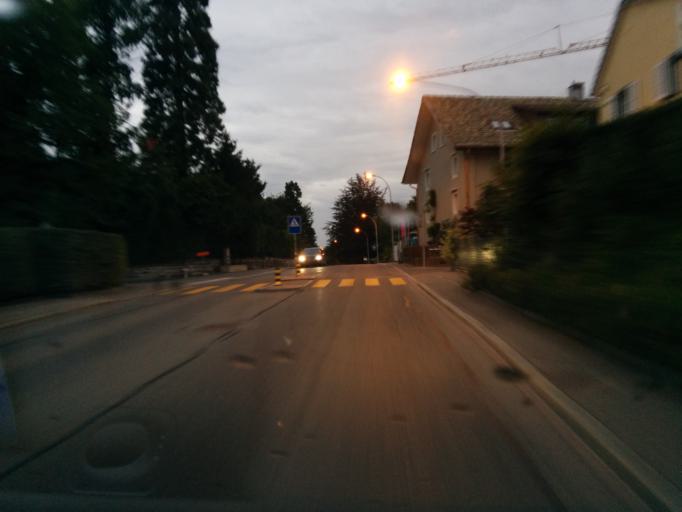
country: CH
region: Zurich
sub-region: Bezirk Meilen
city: Kuesnacht / Goldbach
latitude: 47.3309
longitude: 8.5799
